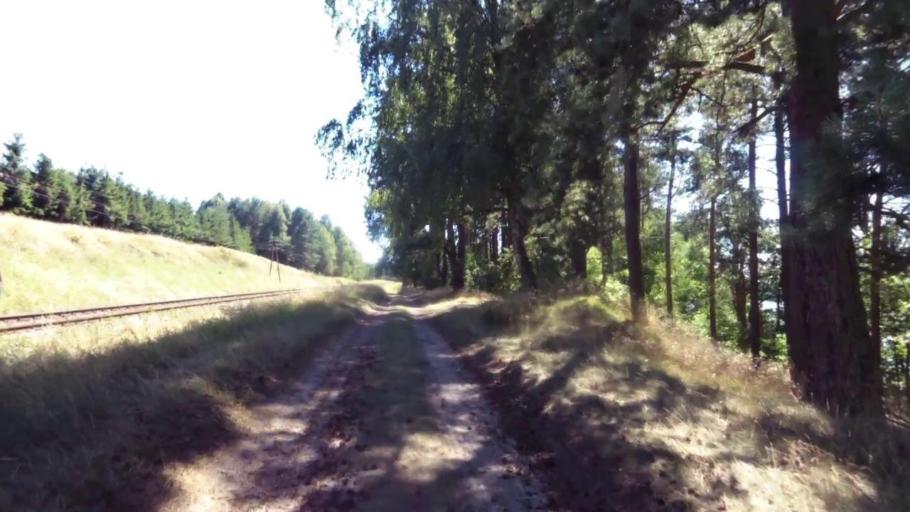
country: PL
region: West Pomeranian Voivodeship
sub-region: Powiat szczecinecki
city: Bialy Bor
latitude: 53.8443
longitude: 16.8729
